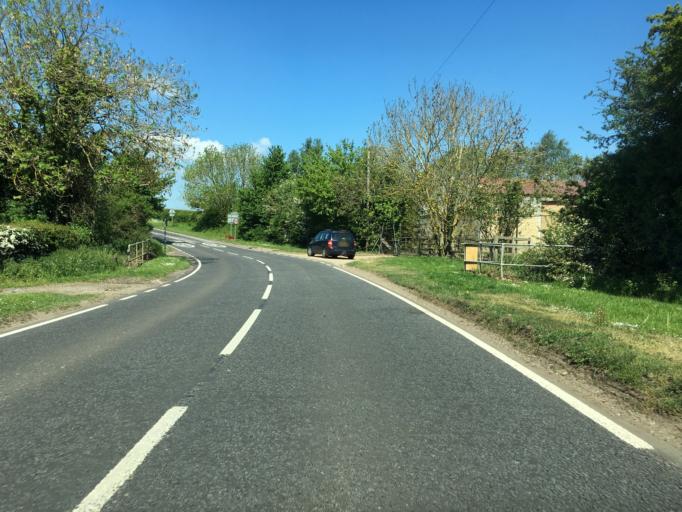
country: GB
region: England
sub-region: Buckinghamshire
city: Buckingham
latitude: 52.0020
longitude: -0.9992
